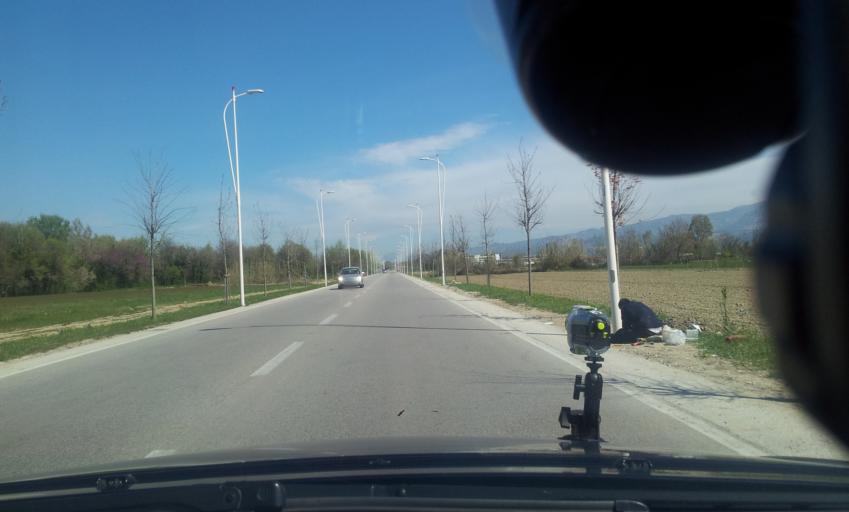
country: AL
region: Tirane
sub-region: Rrethi i Tiranes
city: Berxull
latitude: 41.3932
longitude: 19.7039
